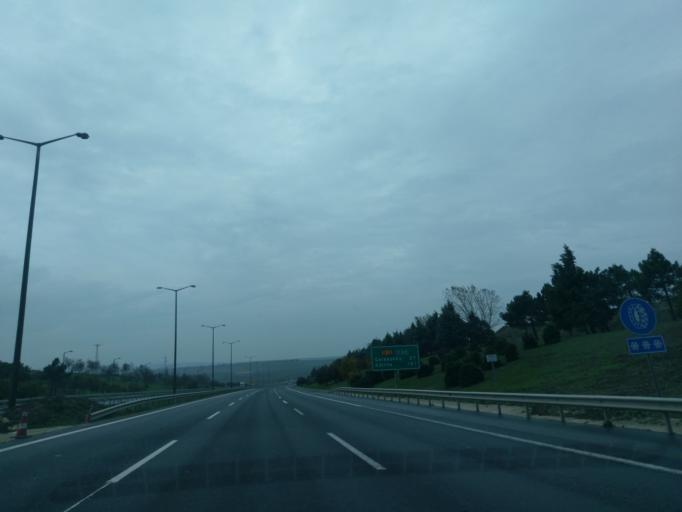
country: TR
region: Istanbul
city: Silivri
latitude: 41.1198
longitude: 28.1812
